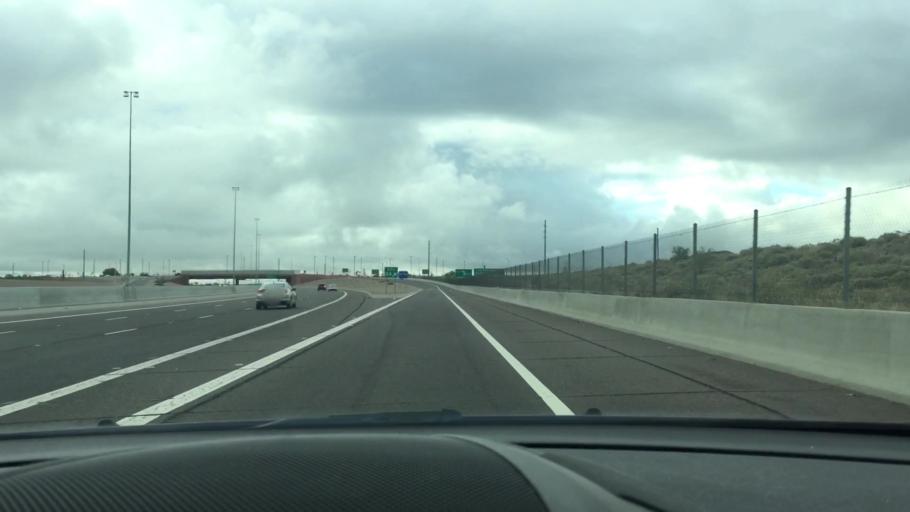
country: US
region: Arizona
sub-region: Pinal County
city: Apache Junction
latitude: 33.4557
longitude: -111.6742
